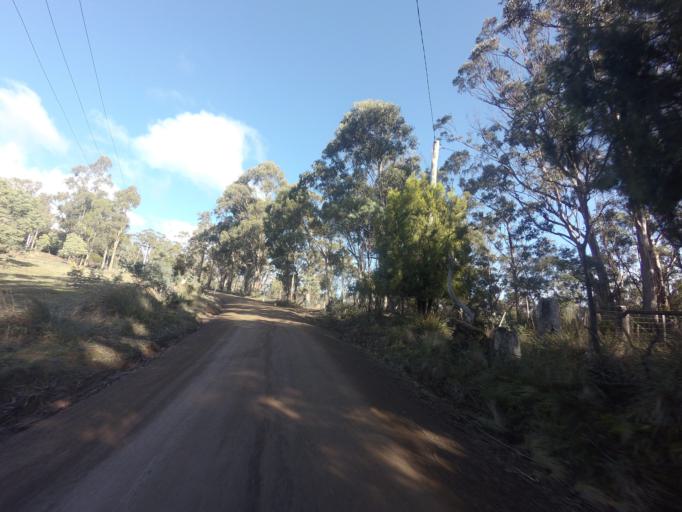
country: AU
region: Tasmania
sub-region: Derwent Valley
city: New Norfolk
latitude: -42.8239
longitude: 147.1187
